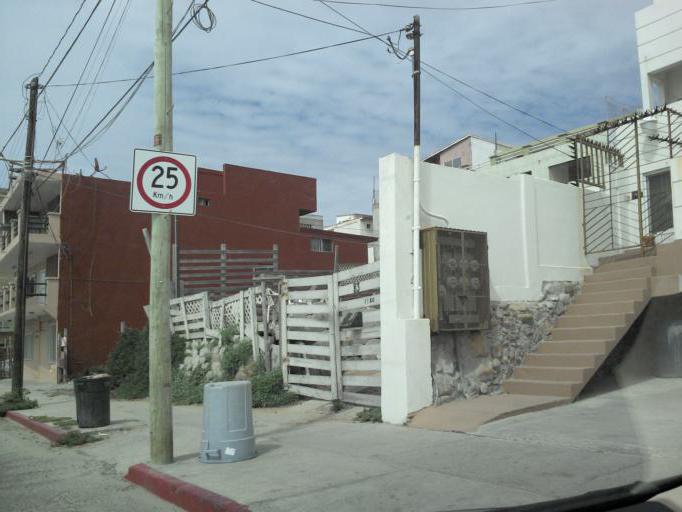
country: US
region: California
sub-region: San Diego County
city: Imperial Beach
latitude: 32.5252
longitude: -117.1239
